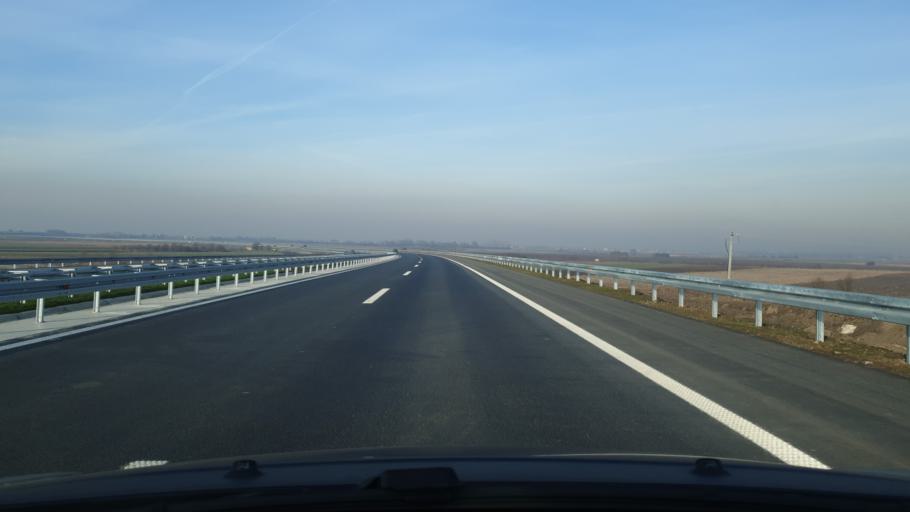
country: RS
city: Boljevci
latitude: 44.7186
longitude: 20.2583
